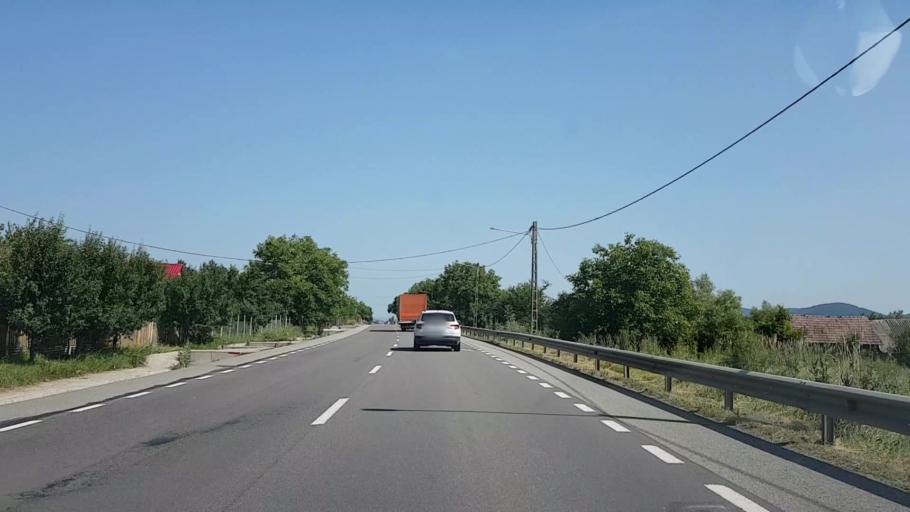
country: RO
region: Bistrita-Nasaud
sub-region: Comuna Sieu-Odorhei
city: Sieu-Odorhei
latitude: 47.1297
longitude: 24.3135
